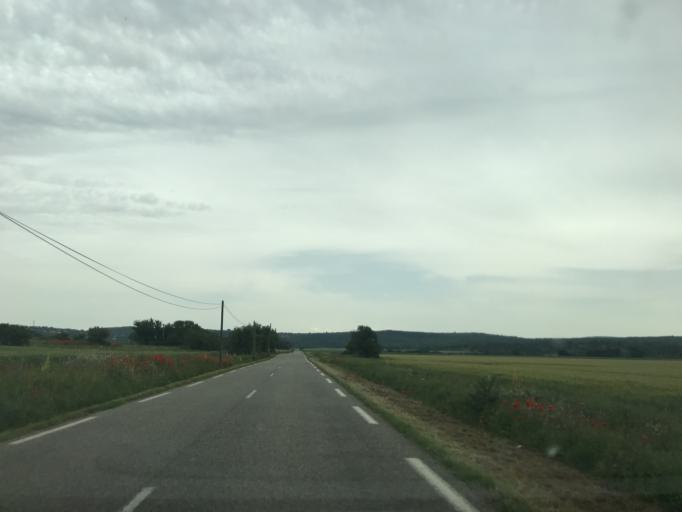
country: FR
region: Provence-Alpes-Cote d'Azur
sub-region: Departement du Var
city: Ginasservis
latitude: 43.6447
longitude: 5.8308
